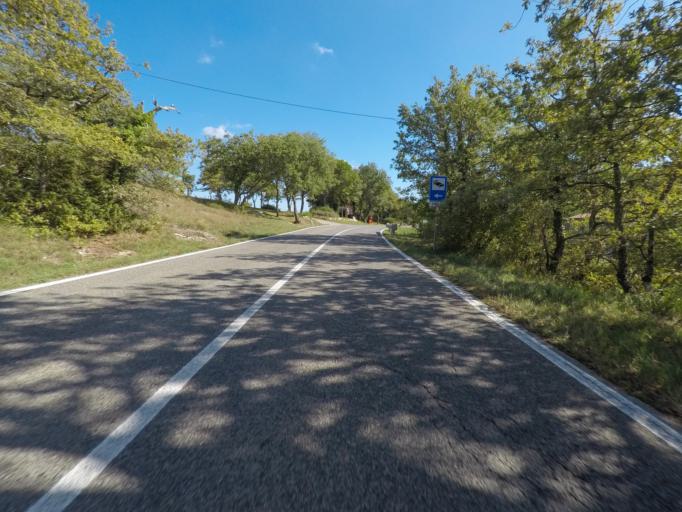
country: IT
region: Tuscany
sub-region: Provincia di Siena
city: Castellina in Chianti
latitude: 43.4843
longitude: 11.3243
